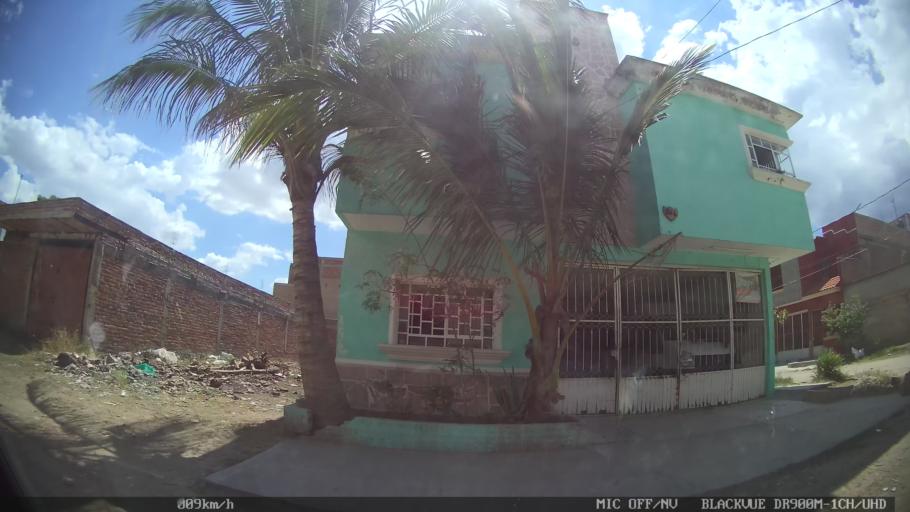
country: MX
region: Jalisco
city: Tlaquepaque
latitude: 20.6685
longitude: -103.2588
